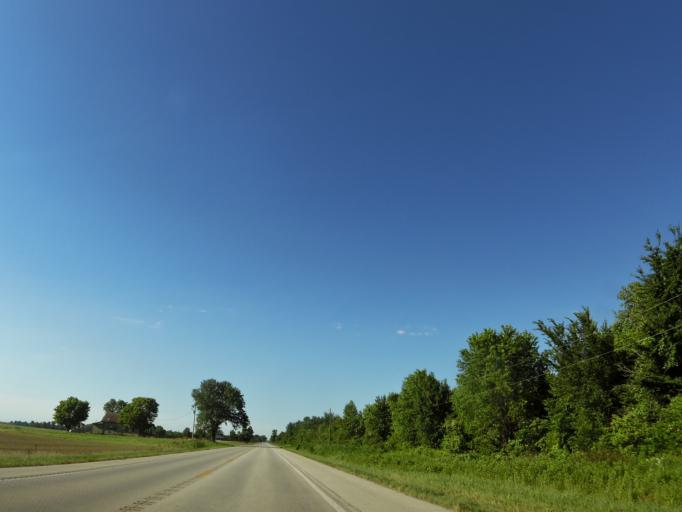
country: US
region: Missouri
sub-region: Butler County
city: Poplar Bluff
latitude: 36.6045
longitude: -90.5205
